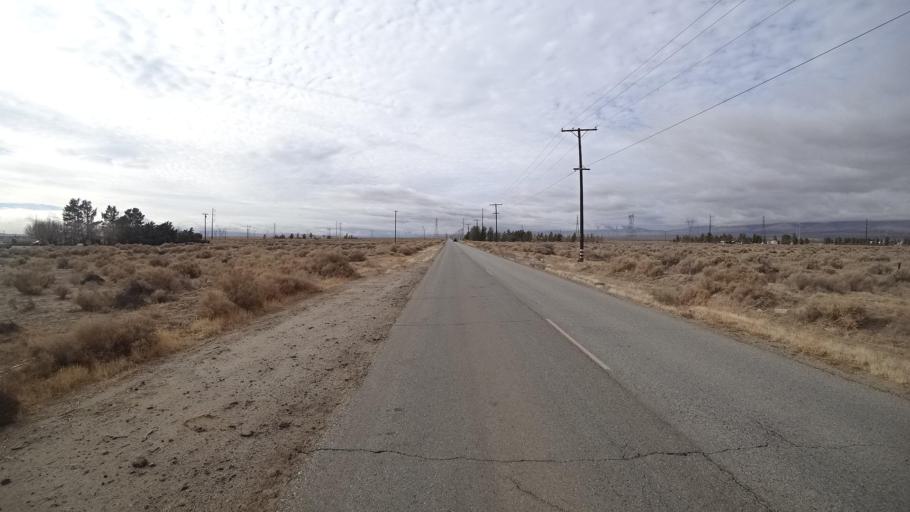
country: US
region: California
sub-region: Kern County
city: Rosamond
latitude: 34.8635
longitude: -118.3052
